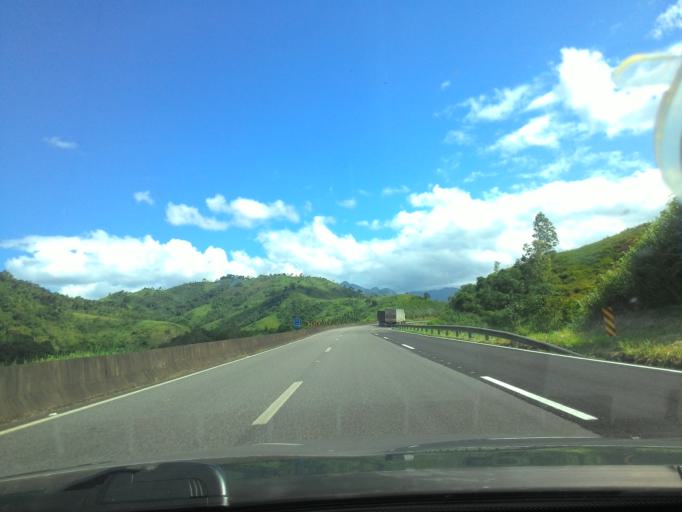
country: BR
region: Sao Paulo
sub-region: Cajati
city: Cajati
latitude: -24.7909
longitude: -48.2107
